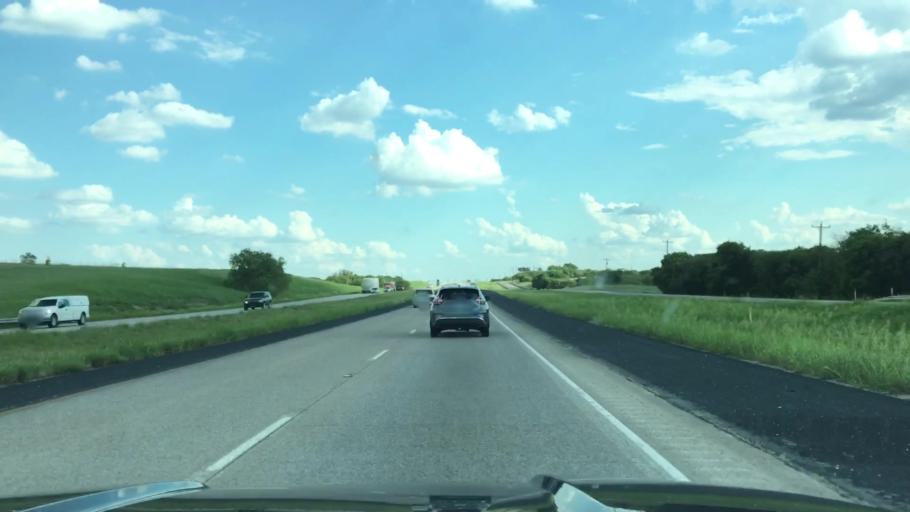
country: US
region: Texas
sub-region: Tarrant County
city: Pecan Acres
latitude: 32.9992
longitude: -97.4338
